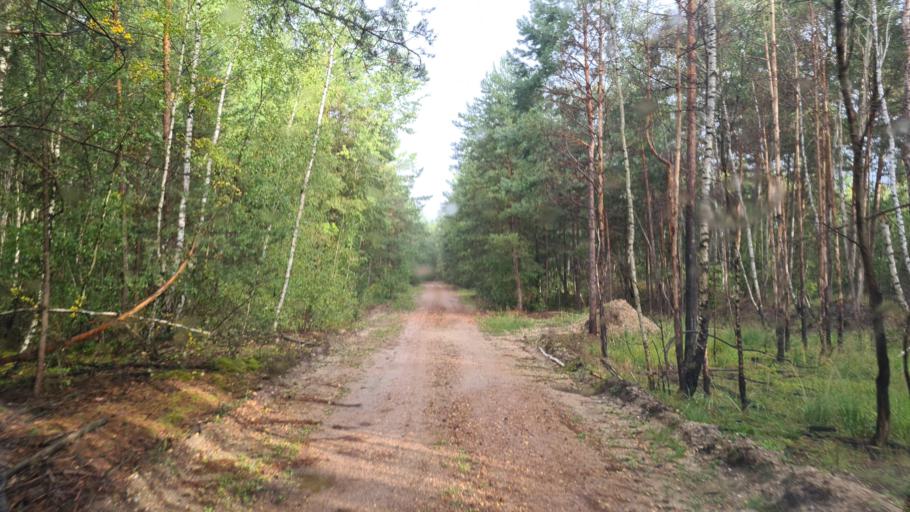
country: DE
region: Brandenburg
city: Sallgast
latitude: 51.5871
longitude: 13.8011
